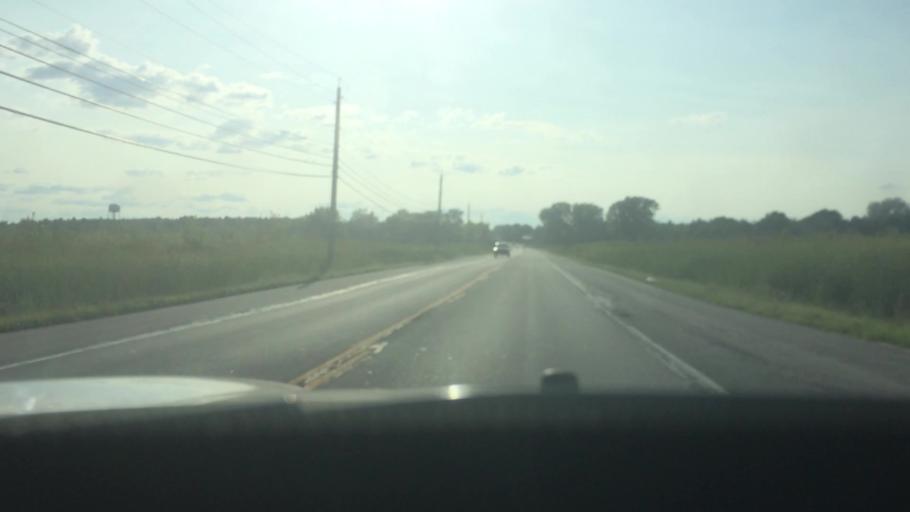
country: US
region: New York
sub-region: St. Lawrence County
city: Potsdam
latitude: 44.6674
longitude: -75.0123
